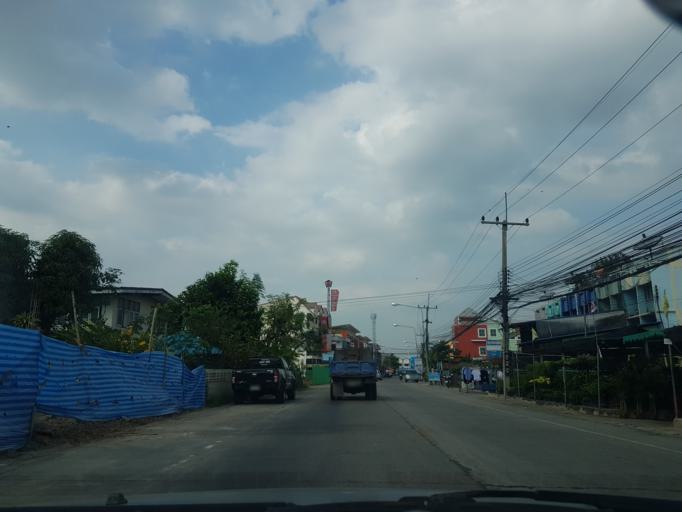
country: TH
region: Phra Nakhon Si Ayutthaya
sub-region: Amphoe Tha Ruea
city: Tha Ruea
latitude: 14.5639
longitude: 100.7196
